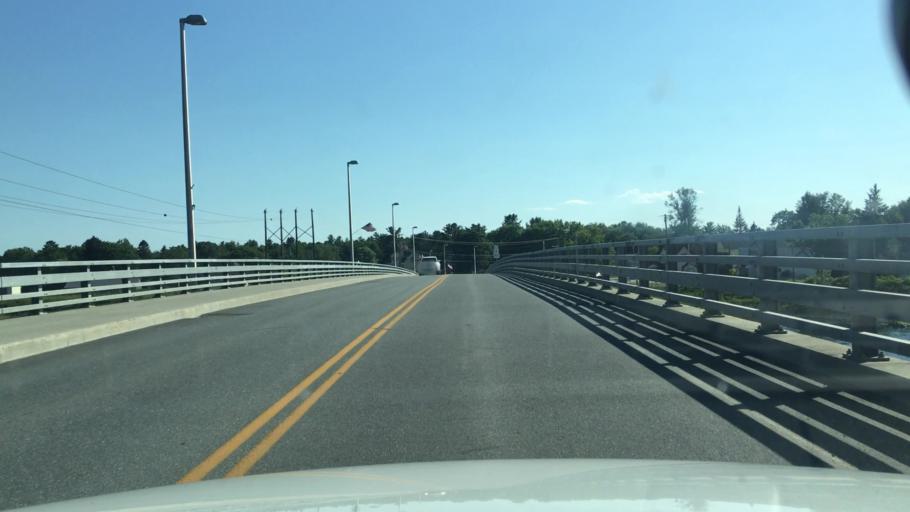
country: US
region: Maine
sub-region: Penobscot County
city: Howland
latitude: 45.2401
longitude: -68.6583
